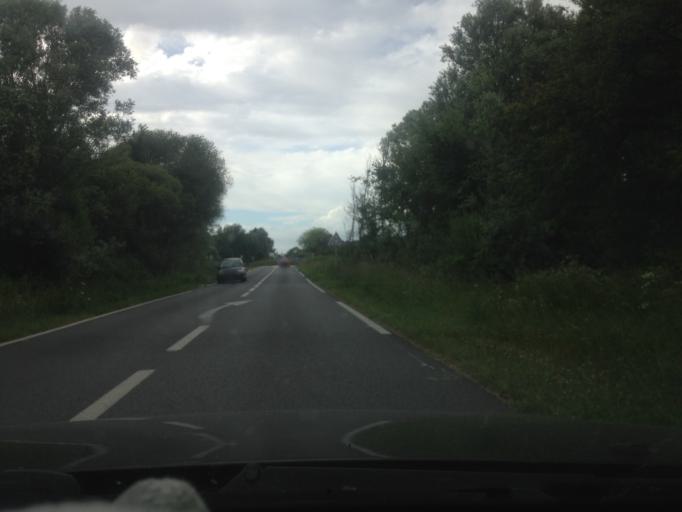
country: FR
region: Brittany
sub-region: Departement du Morbihan
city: Plouharnel
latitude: 47.6122
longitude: -3.1271
